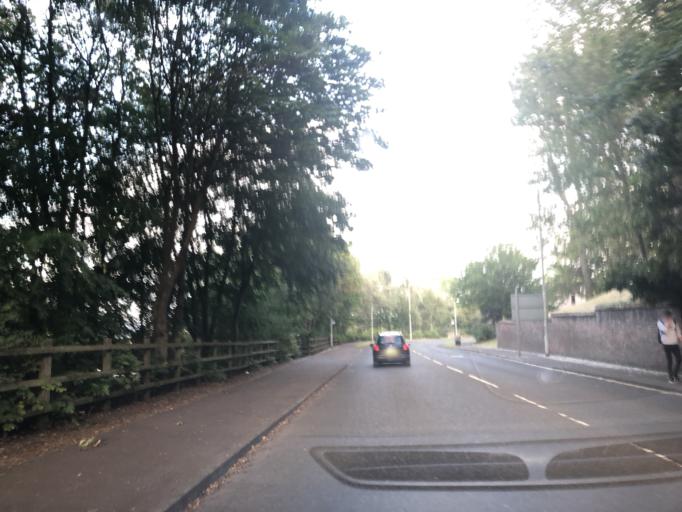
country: GB
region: Scotland
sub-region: Fife
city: Leven
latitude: 56.1920
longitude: -3.0035
